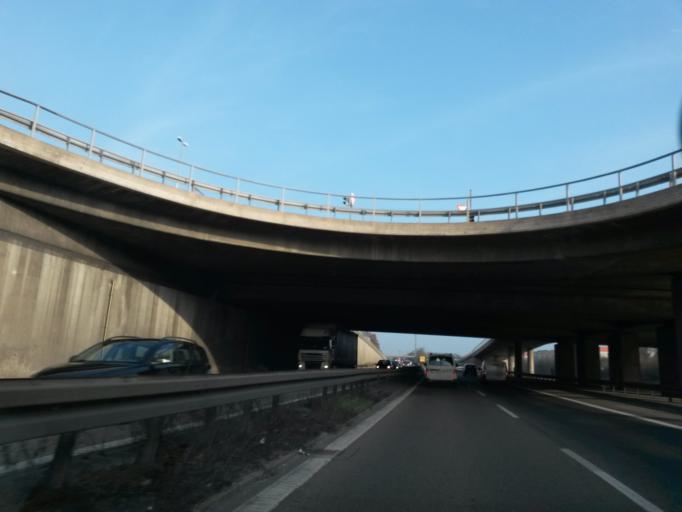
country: DE
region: Bavaria
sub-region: Regierungsbezirk Mittelfranken
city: Grossreuth bei Schweinau
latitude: 49.4233
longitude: 11.0371
